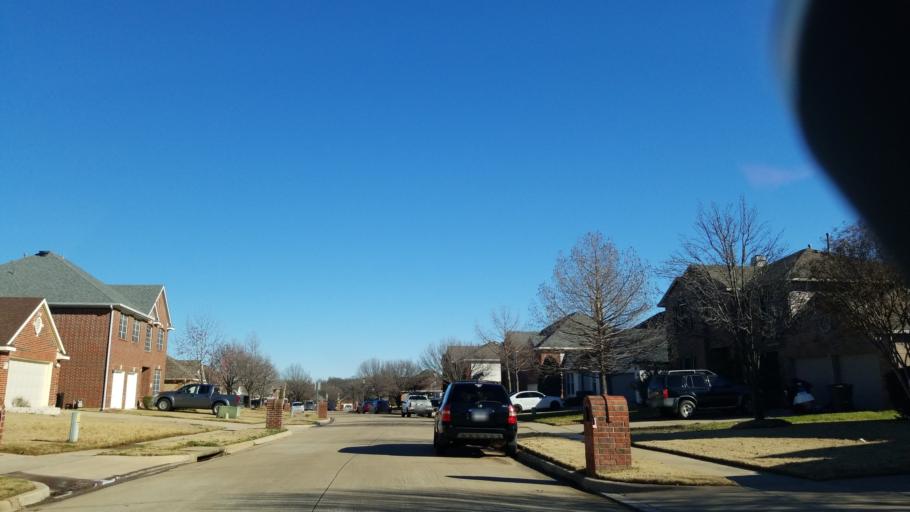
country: US
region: Texas
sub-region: Denton County
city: Corinth
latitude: 33.1428
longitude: -97.0845
